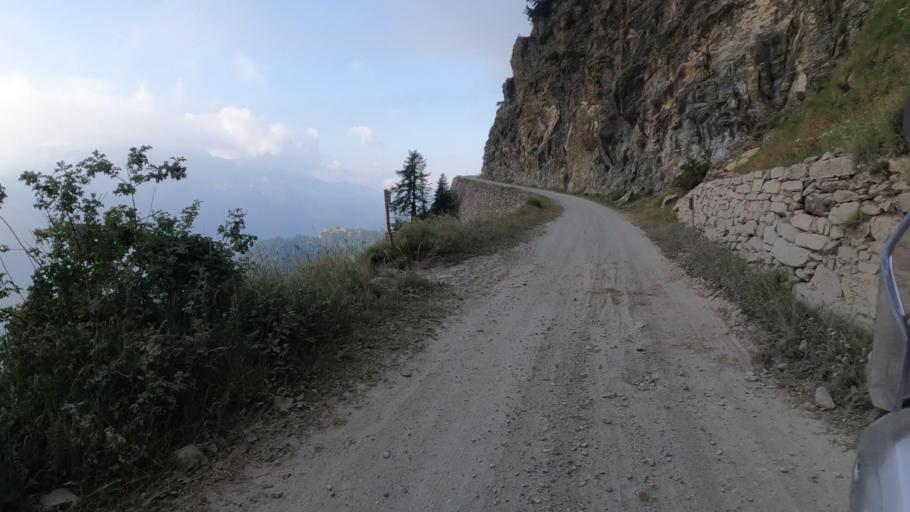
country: IT
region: Piedmont
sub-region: Provincia di Torino
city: Usseaux
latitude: 45.0592
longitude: 6.9848
